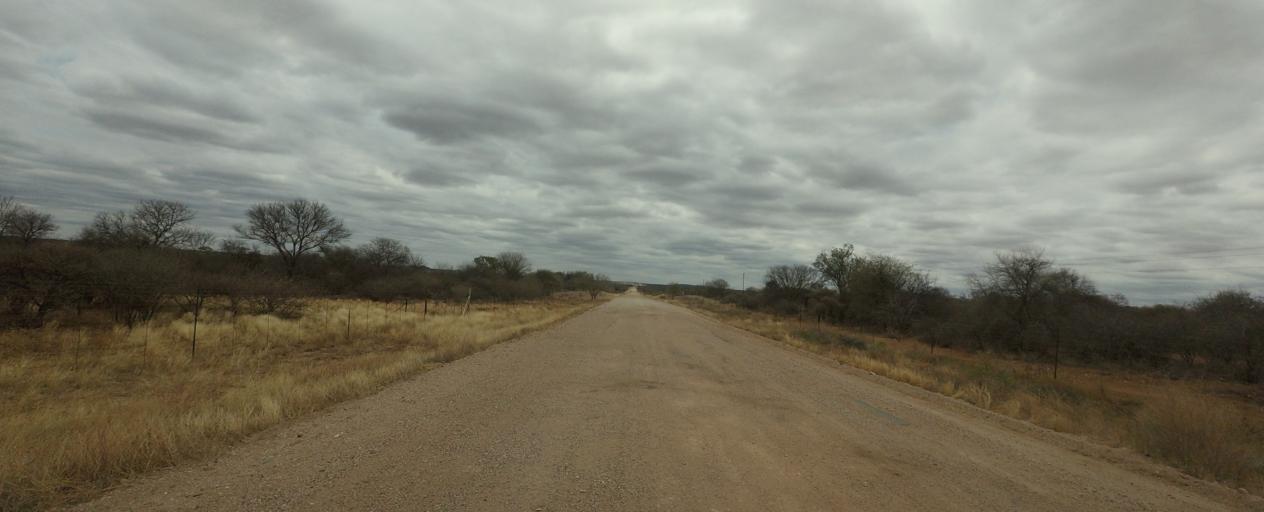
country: BW
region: Central
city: Mathathane
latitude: -22.7048
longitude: 28.6025
